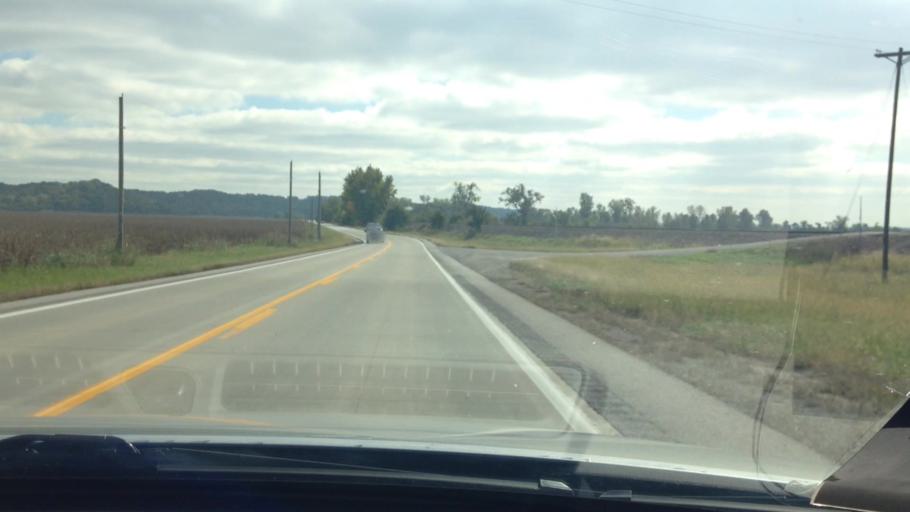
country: US
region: Kansas
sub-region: Leavenworth County
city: Lansing
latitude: 39.2715
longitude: -94.8241
